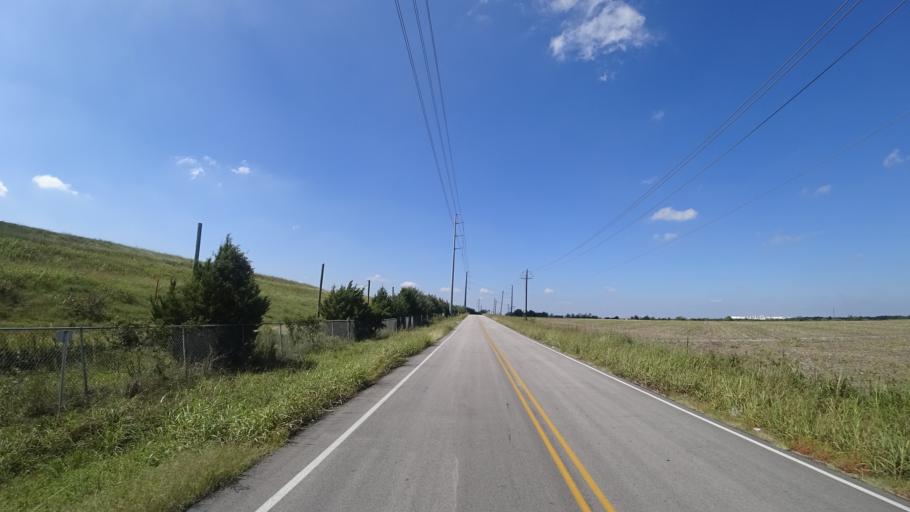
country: US
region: Texas
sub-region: Travis County
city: Manor
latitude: 30.3488
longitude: -97.6279
